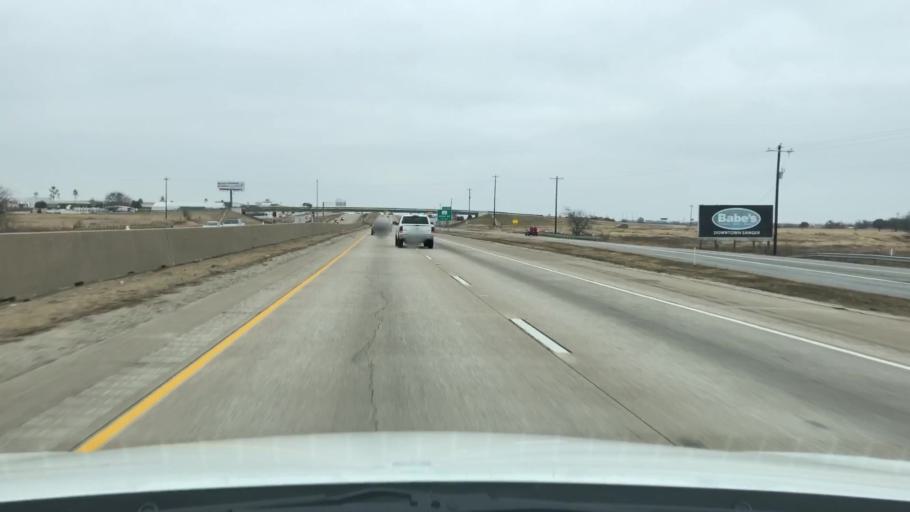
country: US
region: Texas
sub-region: Denton County
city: Krum
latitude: 33.2803
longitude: -97.1779
